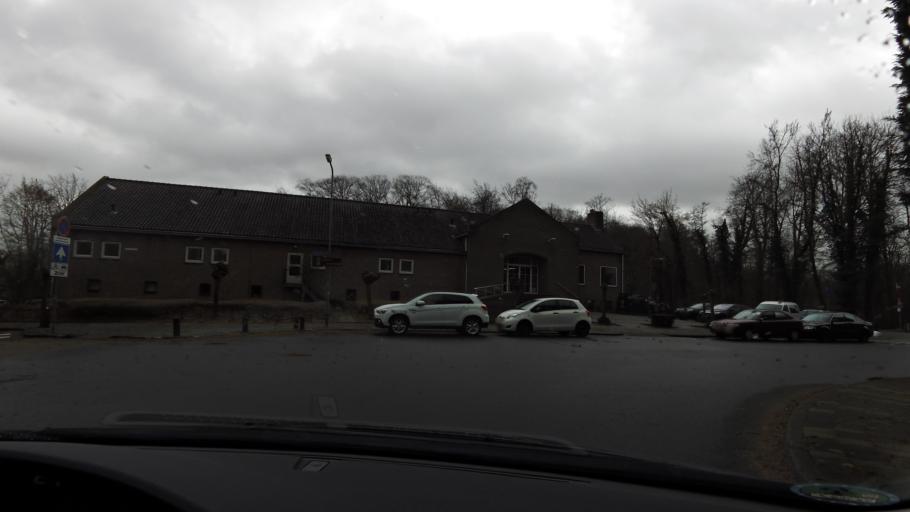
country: NL
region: Limburg
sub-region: Gemeente Beek
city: Beek
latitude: 50.9367
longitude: 5.7903
